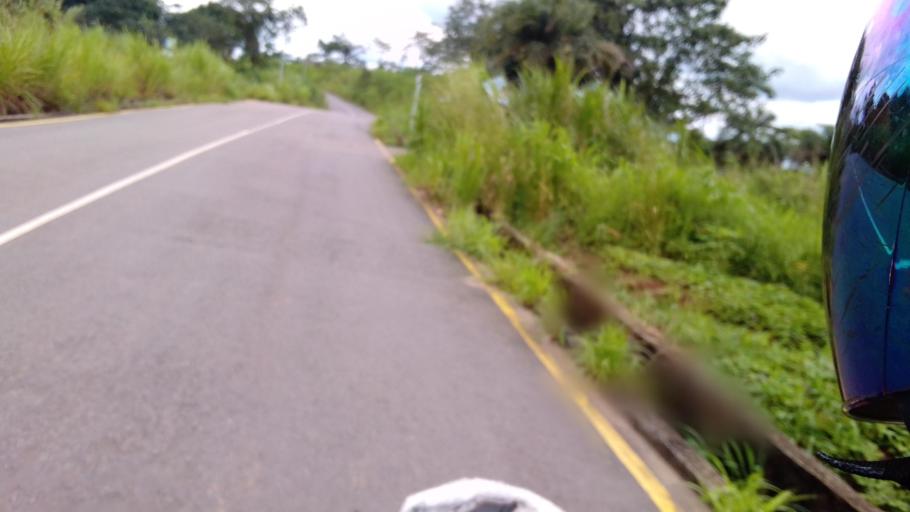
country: SL
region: Eastern Province
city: Koidu
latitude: 8.6589
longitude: -10.9870
